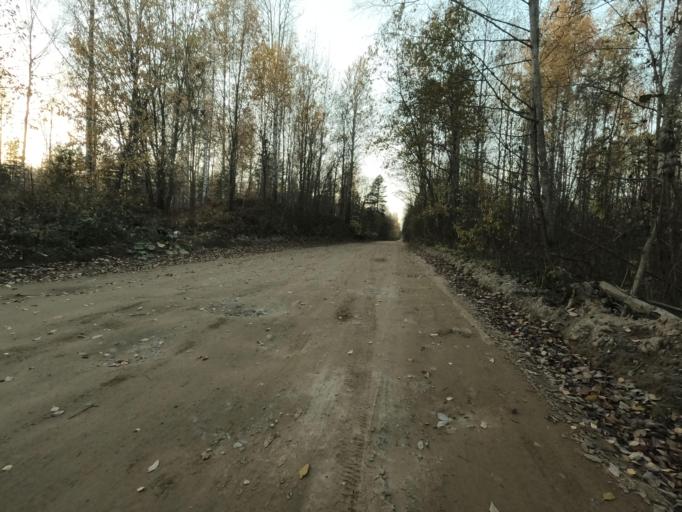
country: RU
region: Leningrad
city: Mga
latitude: 59.7574
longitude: 31.2720
